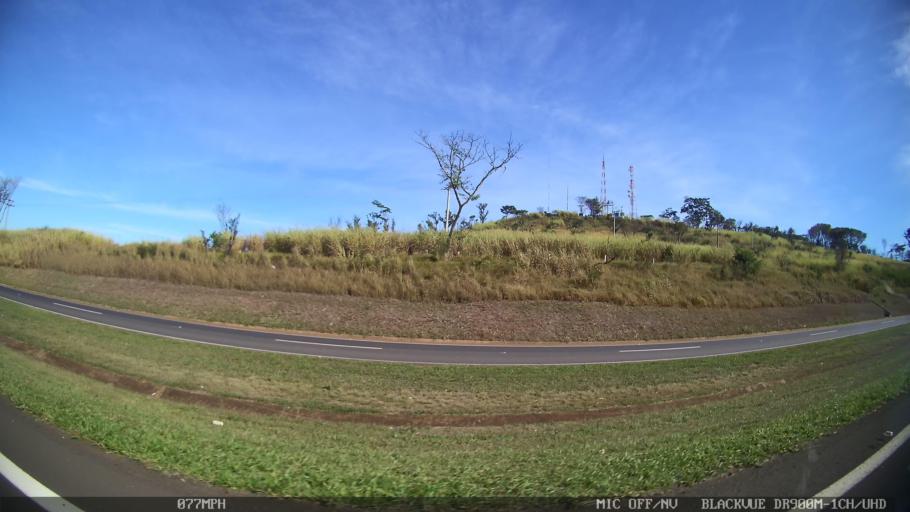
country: BR
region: Sao Paulo
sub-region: Leme
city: Leme
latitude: -22.1588
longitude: -47.3999
